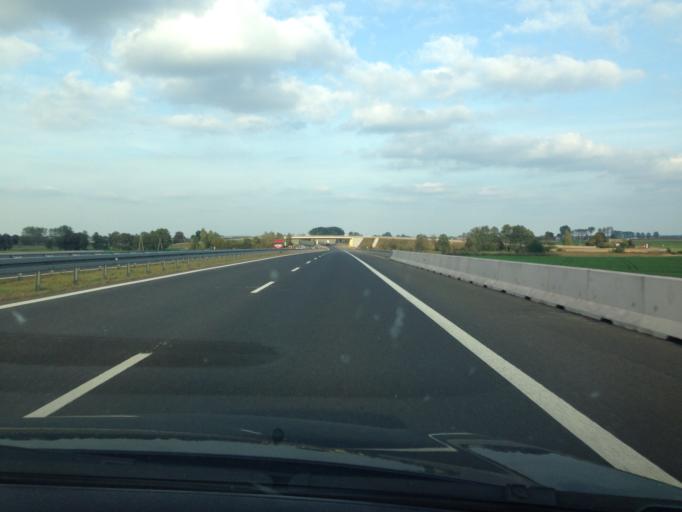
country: PL
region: Greater Poland Voivodeship
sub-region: Powiat gnieznienski
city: Lubowo
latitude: 52.4961
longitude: 17.4520
